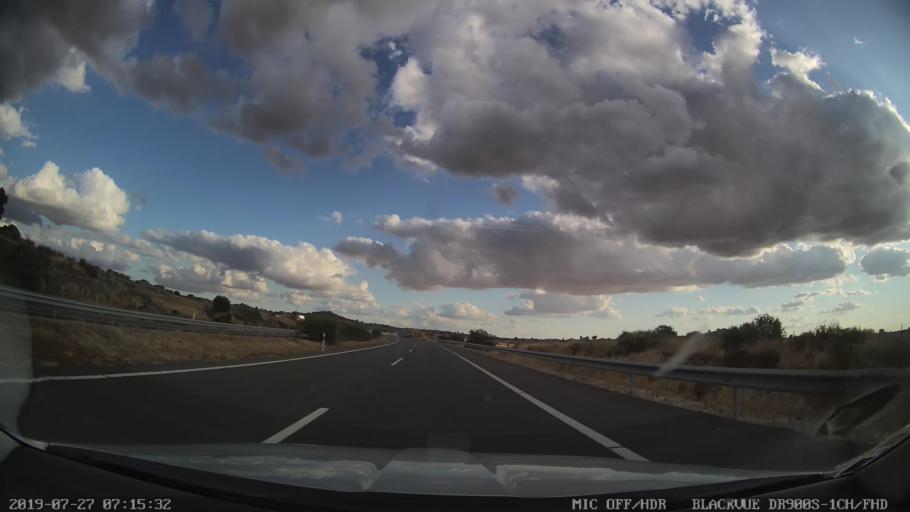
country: ES
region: Extremadura
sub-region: Provincia de Caceres
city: Trujillo
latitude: 39.4736
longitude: -5.8547
